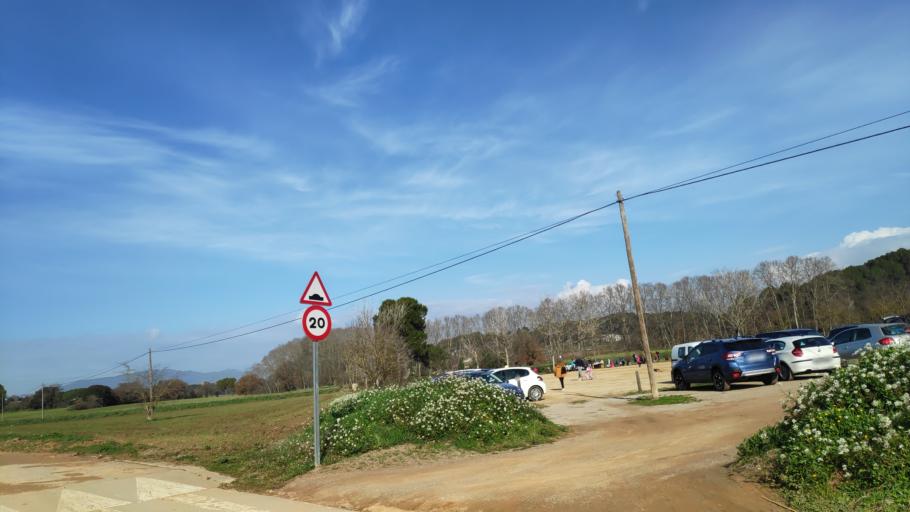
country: ES
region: Catalonia
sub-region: Provincia de Barcelona
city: Mollet del Valles
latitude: 41.5648
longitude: 2.1945
